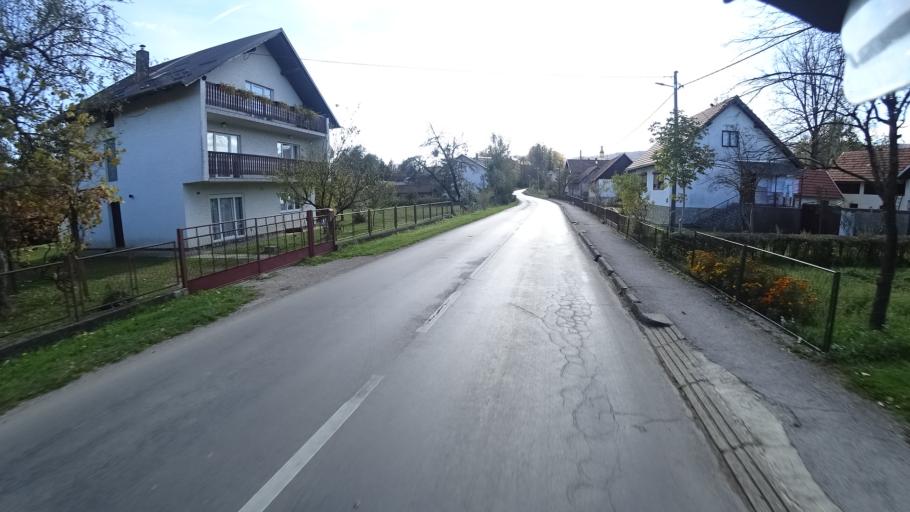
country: HR
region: Karlovacka
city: Plaski
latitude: 45.0862
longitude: 15.3665
